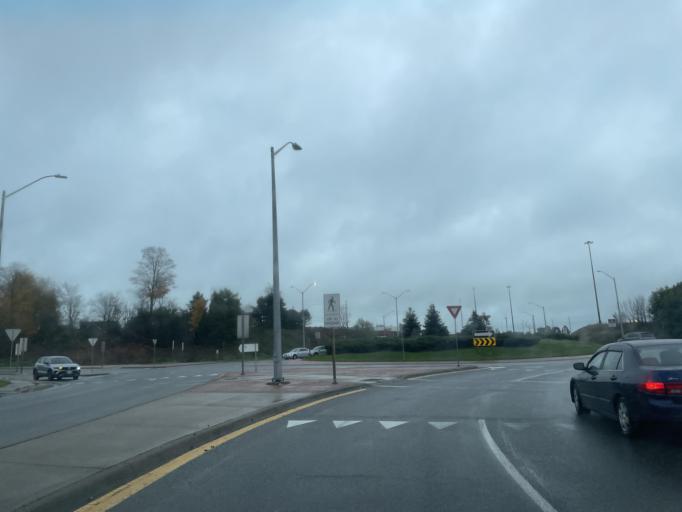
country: CA
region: Ontario
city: Cambridge
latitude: 43.4205
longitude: -80.3291
